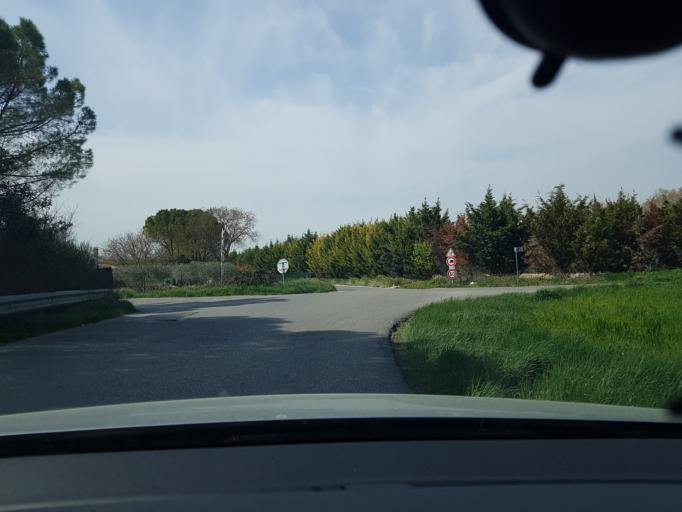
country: FR
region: Provence-Alpes-Cote d'Azur
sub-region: Departement des Bouches-du-Rhone
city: Bouc-Bel-Air
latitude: 43.4751
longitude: 5.3923
